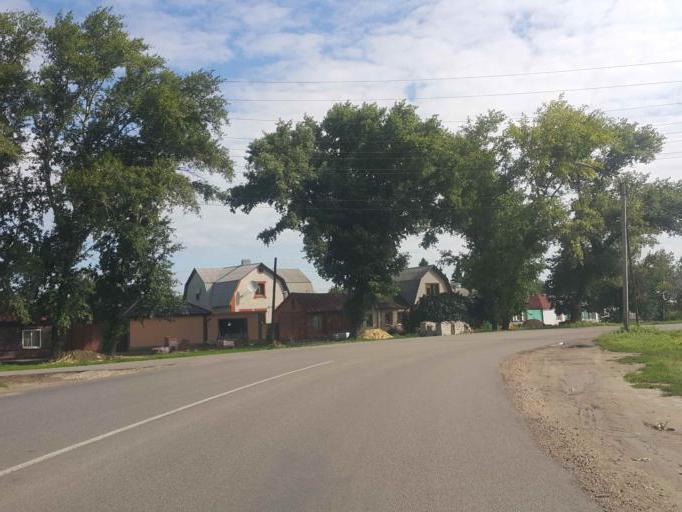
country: RU
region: Tambov
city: Pokrovo-Prigorodnoye
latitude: 52.7132
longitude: 41.4196
